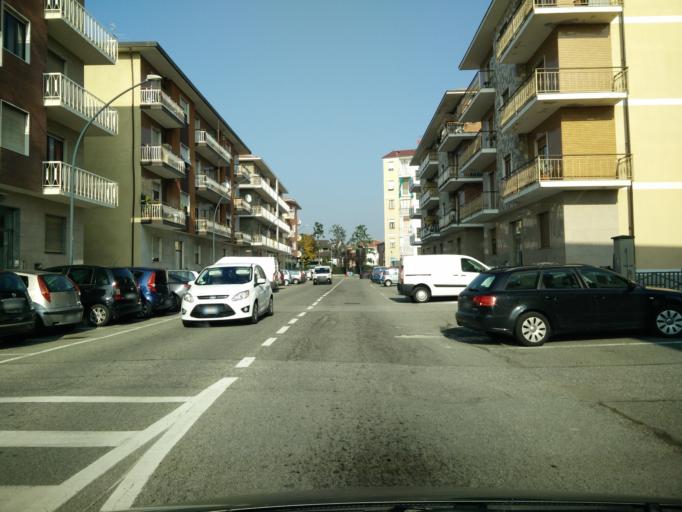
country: IT
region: Piedmont
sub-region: Provincia di Torino
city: Leini
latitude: 45.1815
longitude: 7.7093
